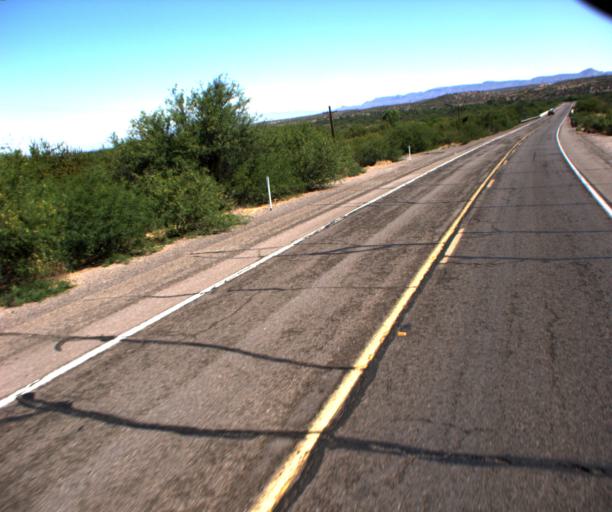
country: US
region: Arizona
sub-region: Pinal County
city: Mammoth
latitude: 32.7402
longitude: -110.6487
